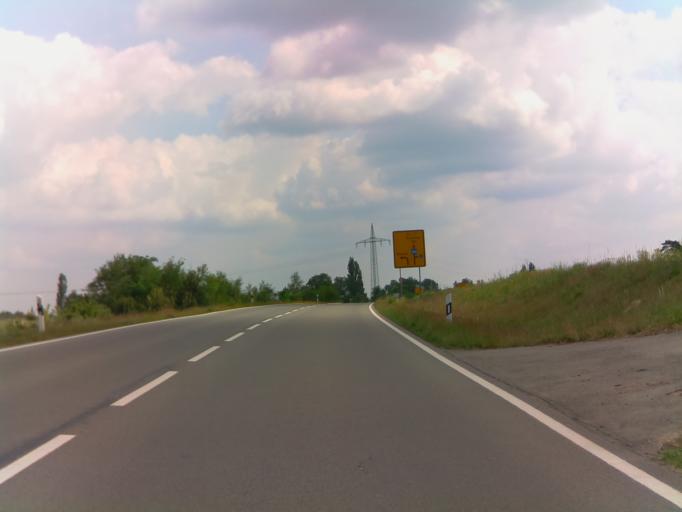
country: DE
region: Brandenburg
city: Rathenow
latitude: 52.5877
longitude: 12.2487
